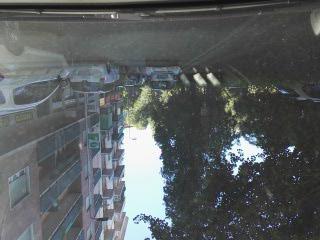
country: IT
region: Lombardy
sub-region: Citta metropolitana di Milano
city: Romano Banco
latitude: 45.4662
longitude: 9.1368
